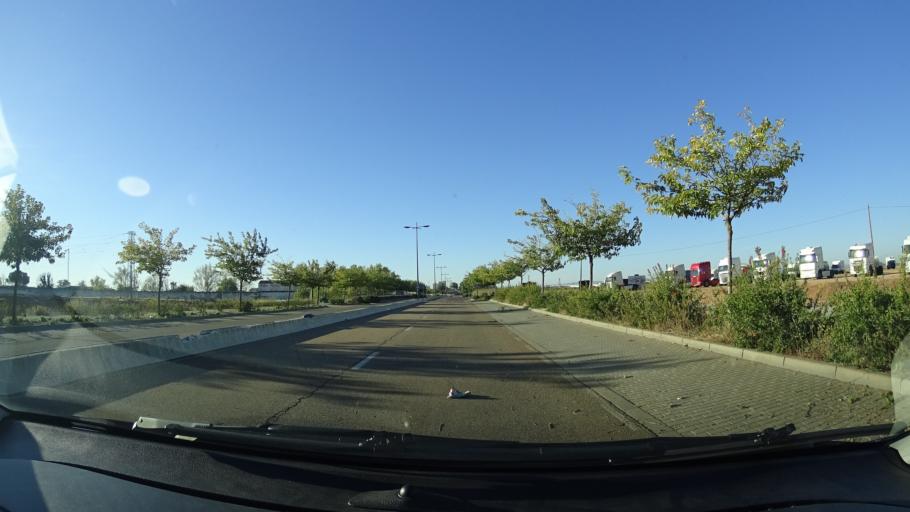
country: ES
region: Extremadura
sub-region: Provincia de Badajoz
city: Almendralejo
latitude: 38.7080
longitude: -6.4003
